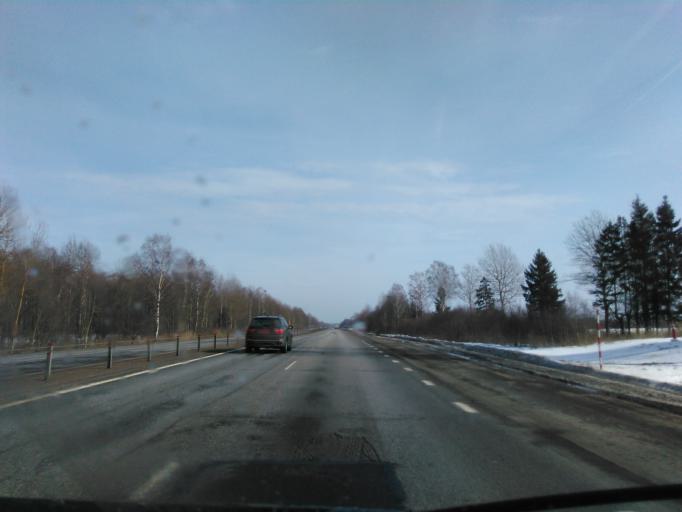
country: BY
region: Vitebsk
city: Dubrowna
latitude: 54.6856
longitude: 30.8242
